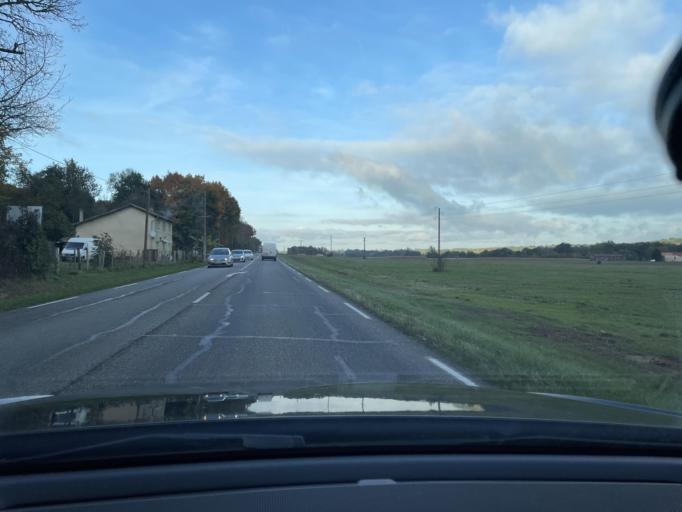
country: FR
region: Aquitaine
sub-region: Departement du Lot-et-Garonne
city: Fourques-sur-Garonne
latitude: 44.3934
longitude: 0.1120
